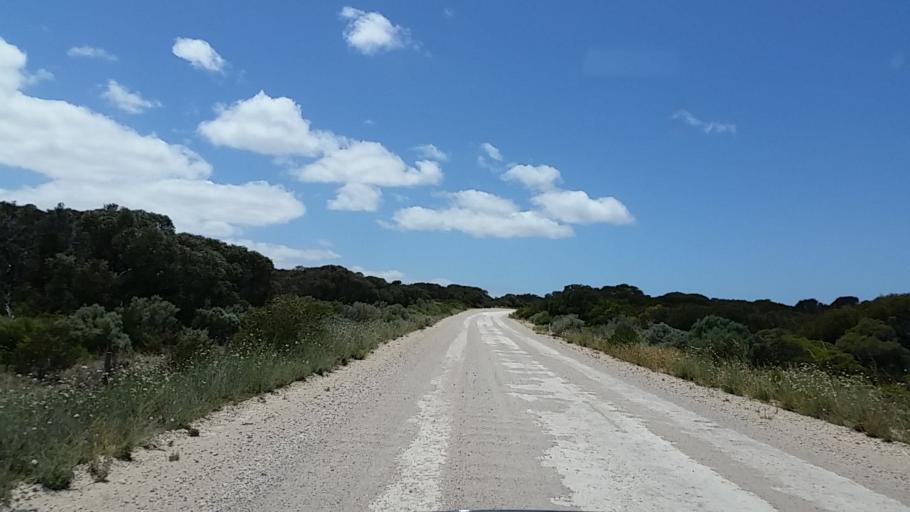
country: AU
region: South Australia
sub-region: Yorke Peninsula
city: Honiton
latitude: -35.2194
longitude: 137.0818
